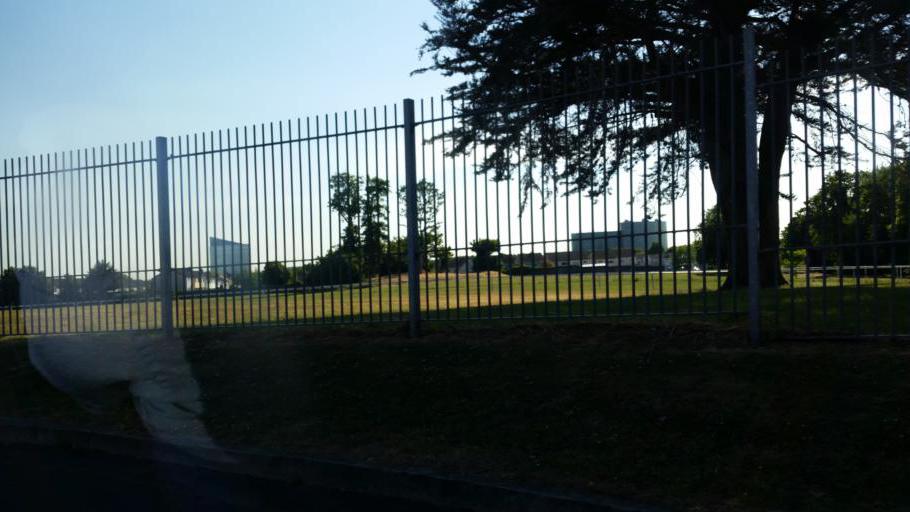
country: IE
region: Leinster
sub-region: Fingal County
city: Blanchardstown
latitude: 53.3987
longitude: -6.3790
